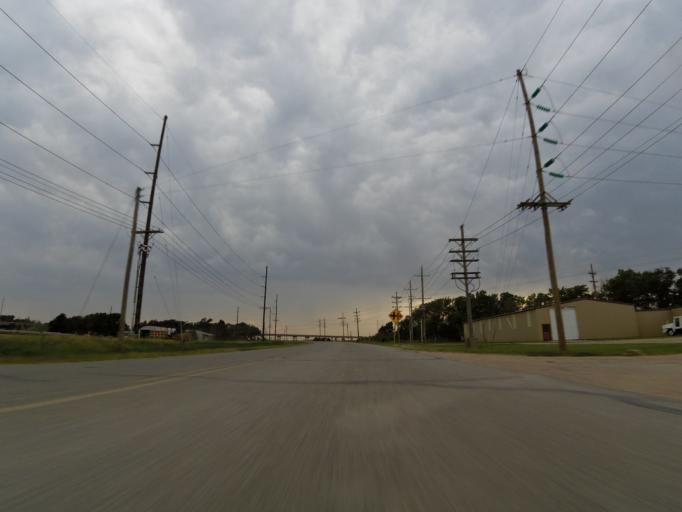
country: US
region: Kansas
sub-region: Reno County
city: South Hutchinson
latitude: 38.0280
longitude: -97.9739
